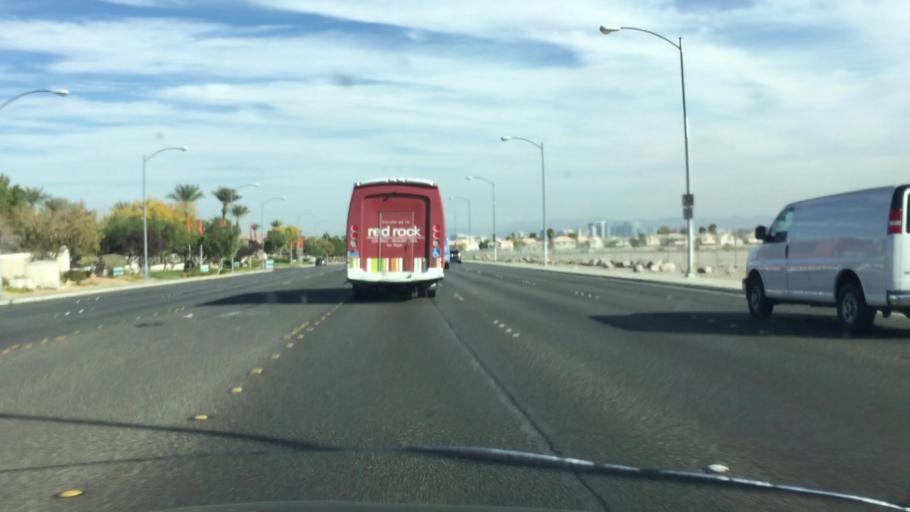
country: US
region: Nevada
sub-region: Clark County
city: Spring Valley
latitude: 36.1295
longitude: -115.2744
